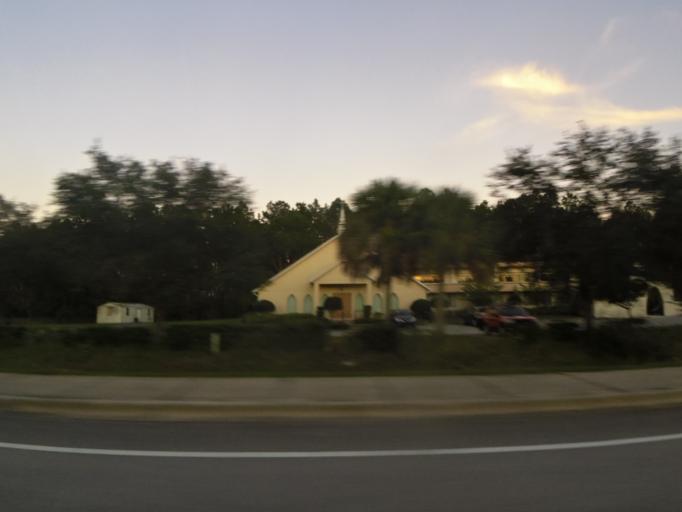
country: US
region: Florida
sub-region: Flagler County
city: Palm Coast
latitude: 29.5786
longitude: -81.2550
